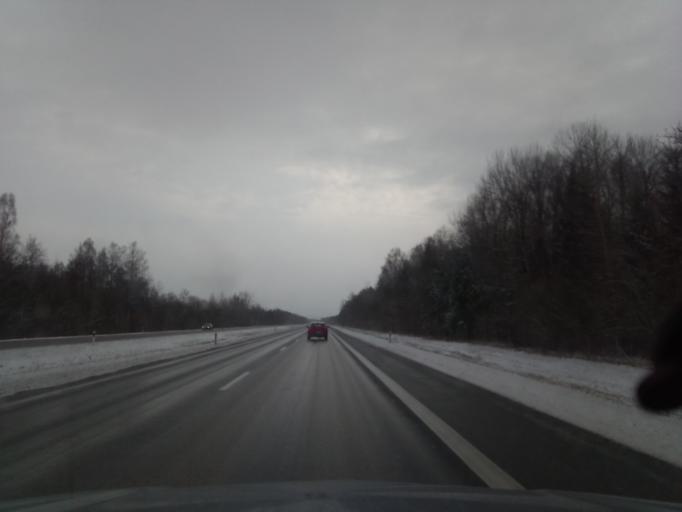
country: LT
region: Panevezys
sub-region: Panevezys City
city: Panevezys
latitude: 55.6408
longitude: 24.3958
